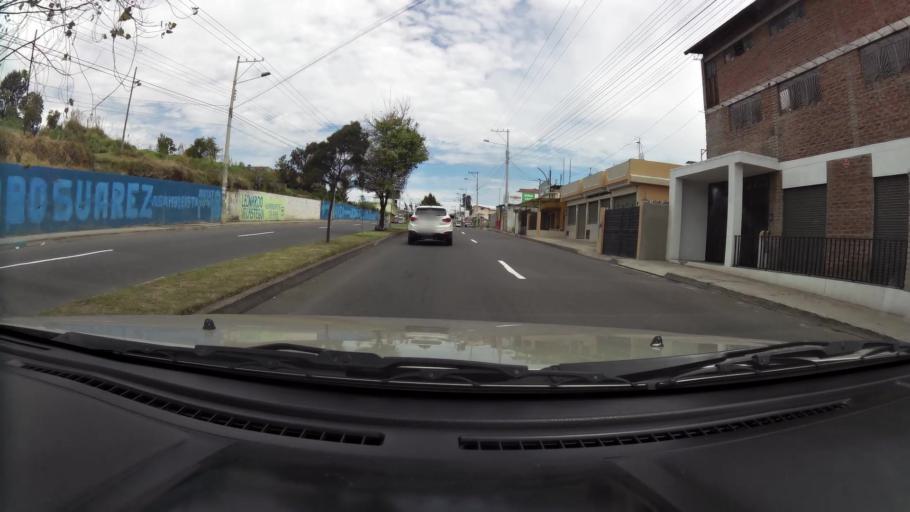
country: EC
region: Cotopaxi
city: San Miguel de Salcedo
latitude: -1.0870
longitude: -78.5938
